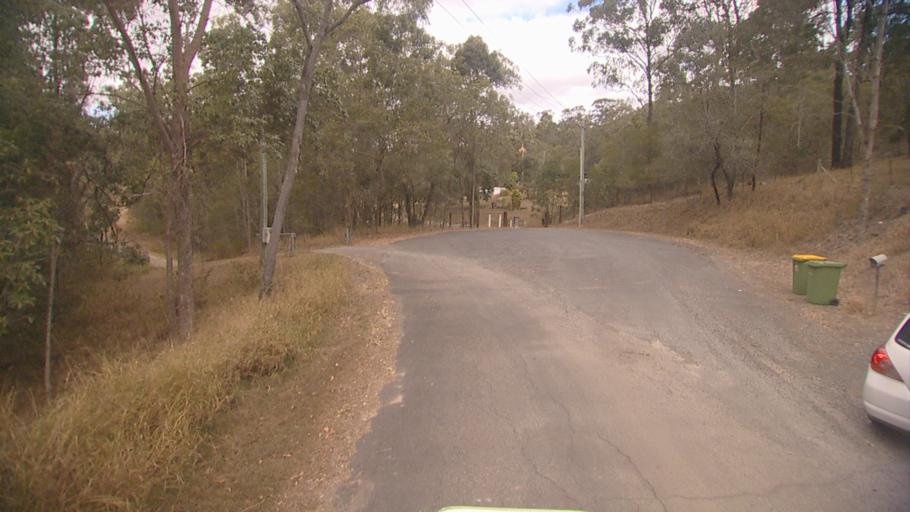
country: AU
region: Queensland
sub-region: Logan
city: Cedar Vale
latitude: -27.8865
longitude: 153.0345
